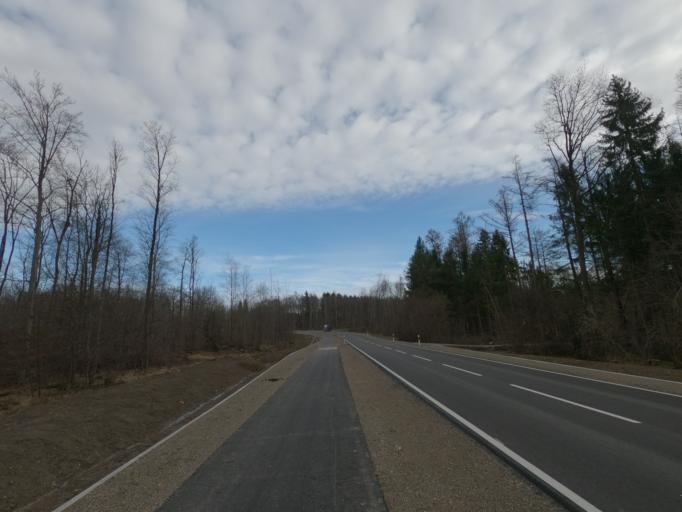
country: DE
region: Baden-Wuerttemberg
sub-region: Regierungsbezirk Stuttgart
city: Ohmden
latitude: 48.6560
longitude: 9.5276
